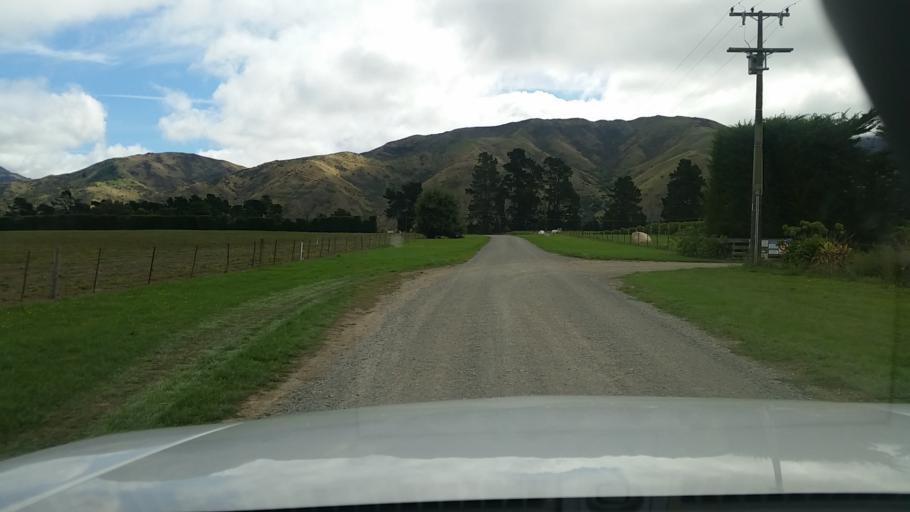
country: NZ
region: Marlborough
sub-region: Marlborough District
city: Blenheim
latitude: -41.6972
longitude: 173.9506
